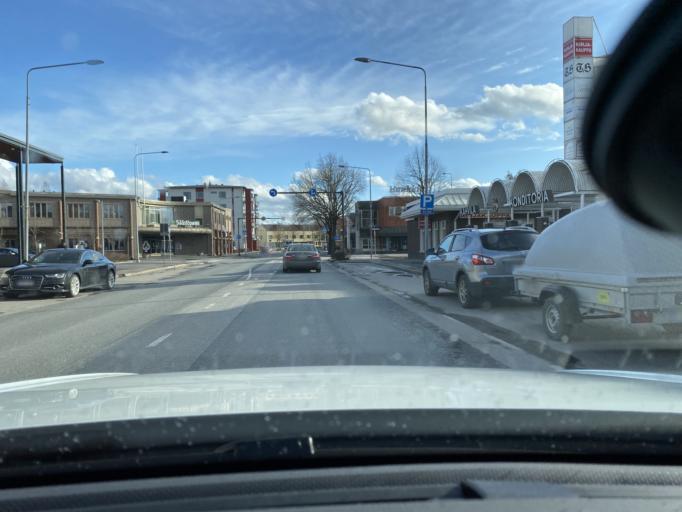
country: FI
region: Satakunta
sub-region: Pori
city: Huittinen
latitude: 61.1780
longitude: 22.6972
